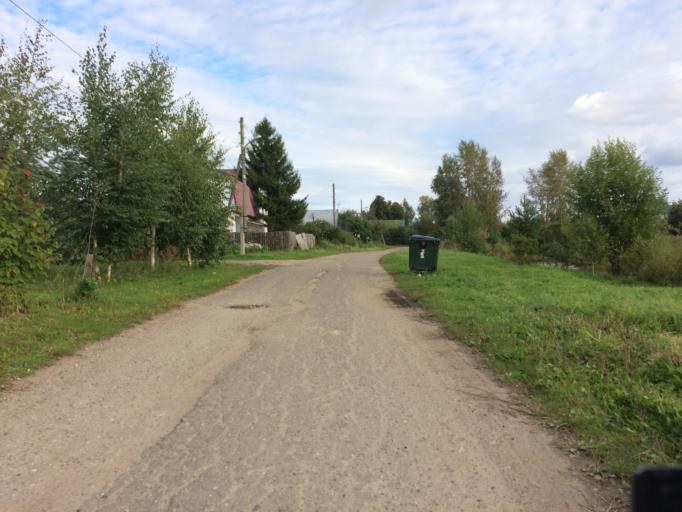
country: RU
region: Mariy-El
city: Yoshkar-Ola
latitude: 56.6539
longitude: 48.0134
